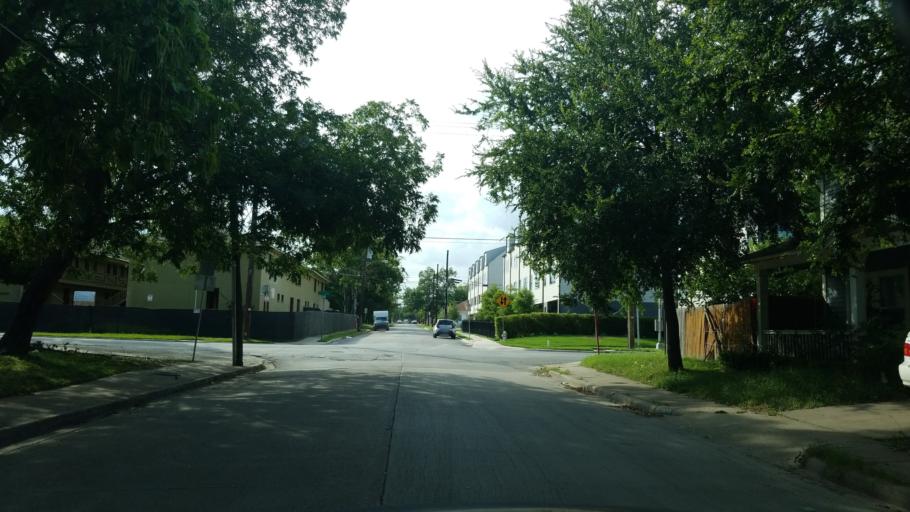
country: US
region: Texas
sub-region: Dallas County
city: Highland Park
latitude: 32.8024
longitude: -96.7748
